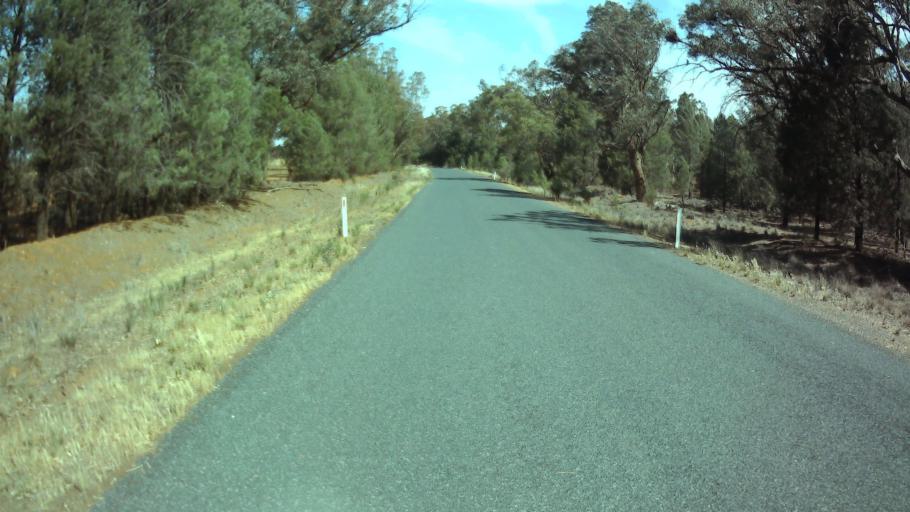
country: AU
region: New South Wales
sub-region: Weddin
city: Grenfell
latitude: -34.0567
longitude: 148.1304
